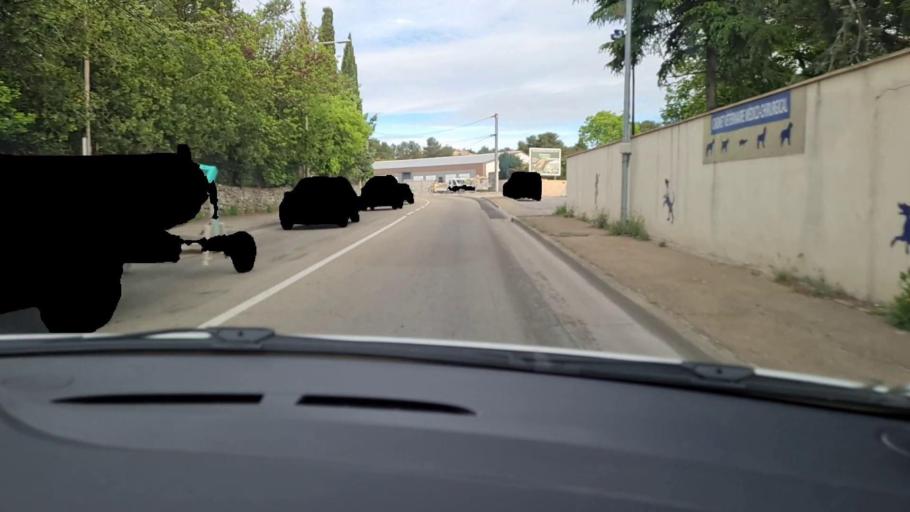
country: FR
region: Languedoc-Roussillon
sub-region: Departement du Gard
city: Nimes
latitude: 43.8420
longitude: 4.3132
